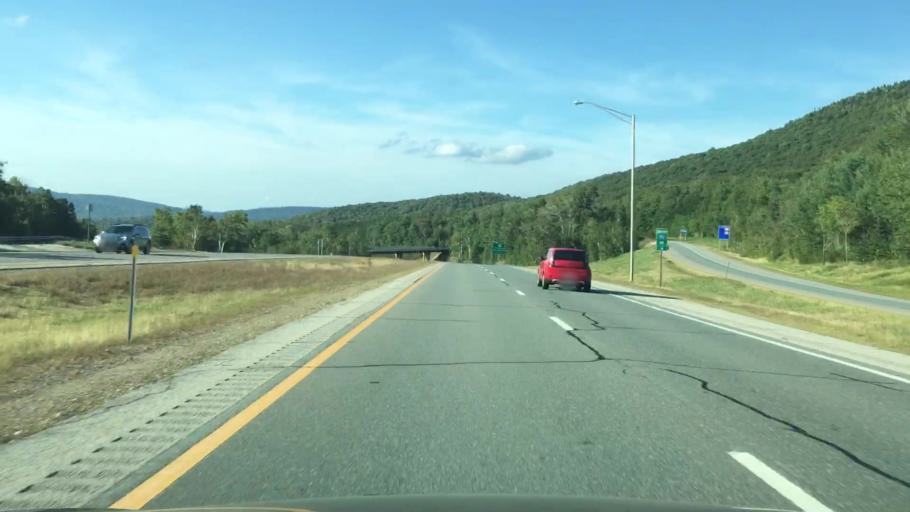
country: US
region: New Hampshire
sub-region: Grafton County
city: Deerfield
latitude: 44.1951
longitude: -71.6814
